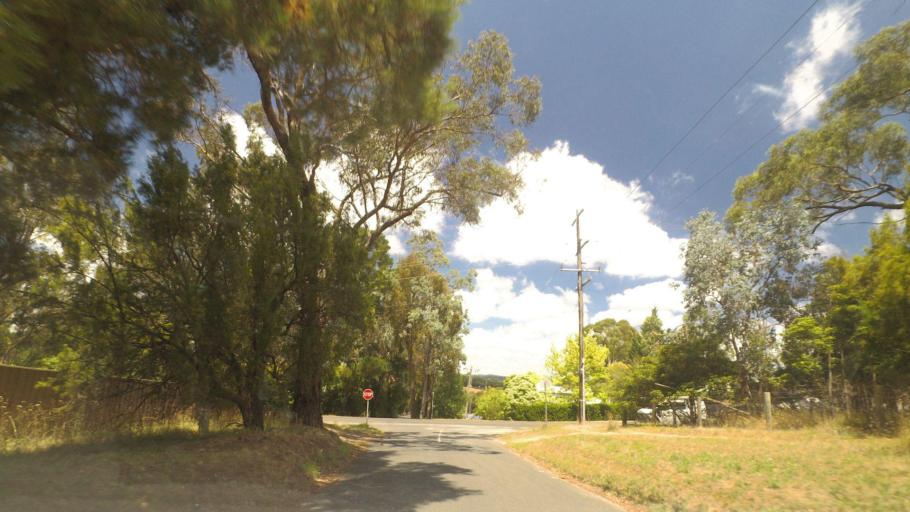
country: AU
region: Victoria
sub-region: Manningham
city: Warrandyte
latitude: -37.7338
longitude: 145.2646
